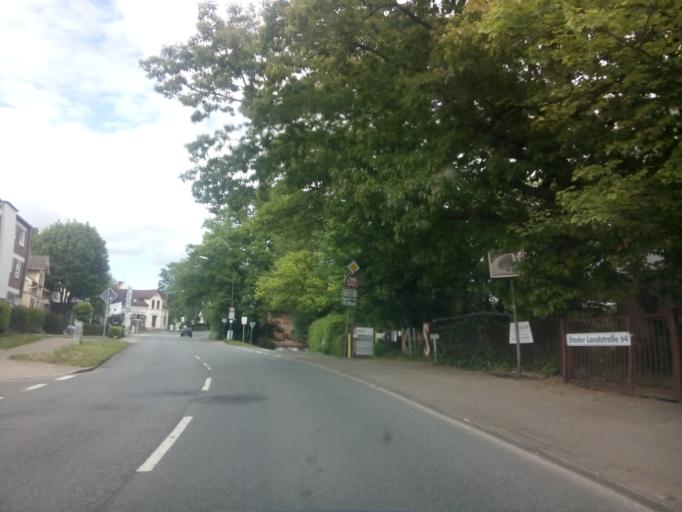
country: DE
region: Lower Saxony
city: Ritterhude
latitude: 53.1687
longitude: 8.7123
